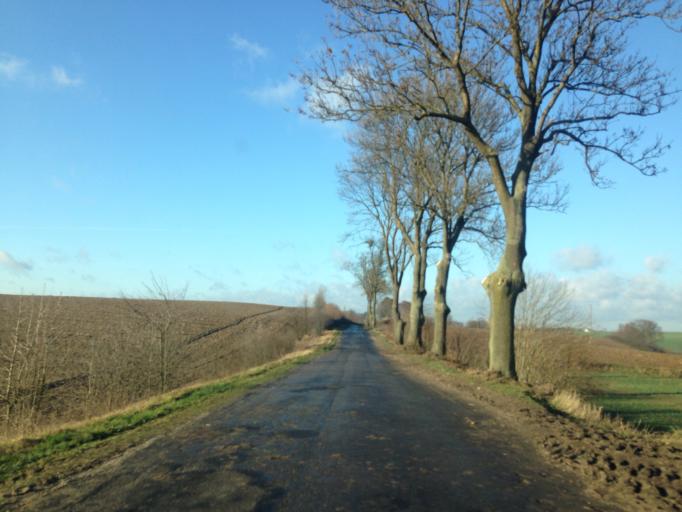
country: PL
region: Kujawsko-Pomorskie
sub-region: Powiat grudziadzki
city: Swiecie nad Osa
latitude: 53.4615
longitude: 19.1572
